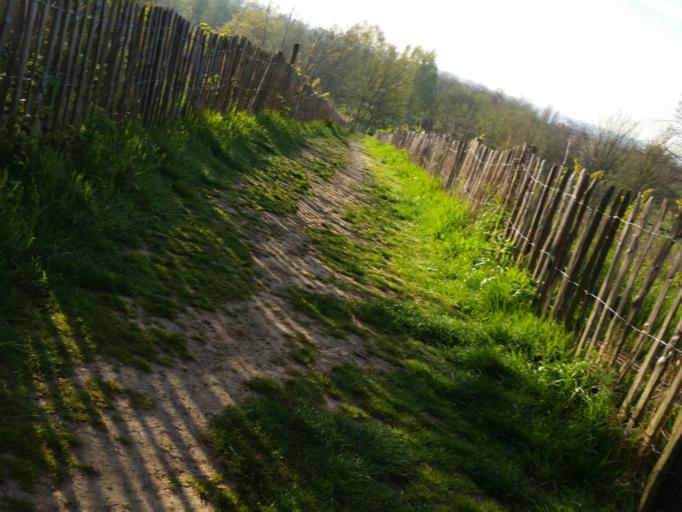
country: BE
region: Flanders
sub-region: Provincie Vlaams-Brabant
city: Grimbergen
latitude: 50.9019
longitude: 4.3894
